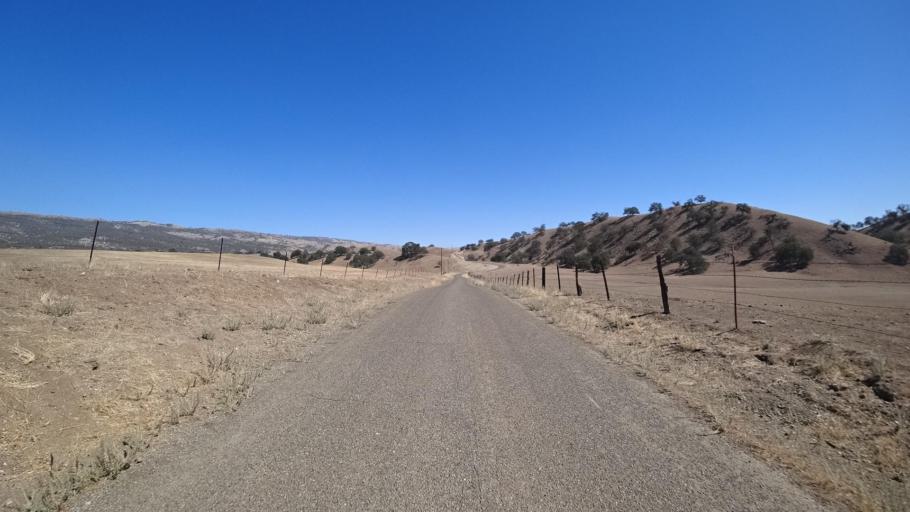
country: US
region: California
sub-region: San Luis Obispo County
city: Shandon
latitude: 35.8777
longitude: -120.3740
